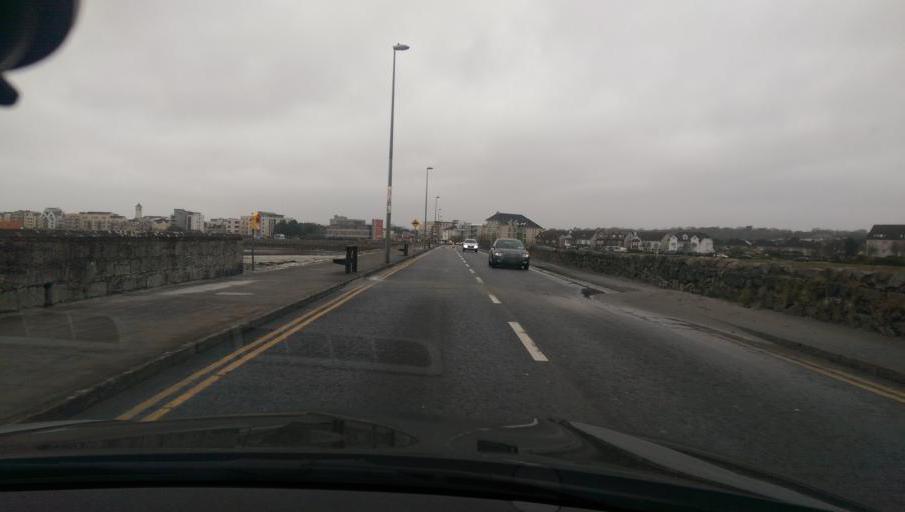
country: IE
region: Connaught
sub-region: County Galway
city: Gaillimh
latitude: 53.2632
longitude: -9.0650
